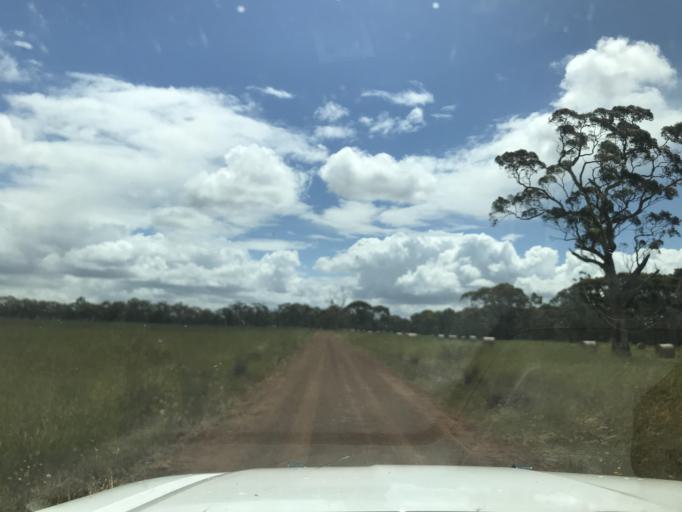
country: AU
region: South Australia
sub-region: Wattle Range
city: Penola
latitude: -37.1235
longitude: 141.2810
